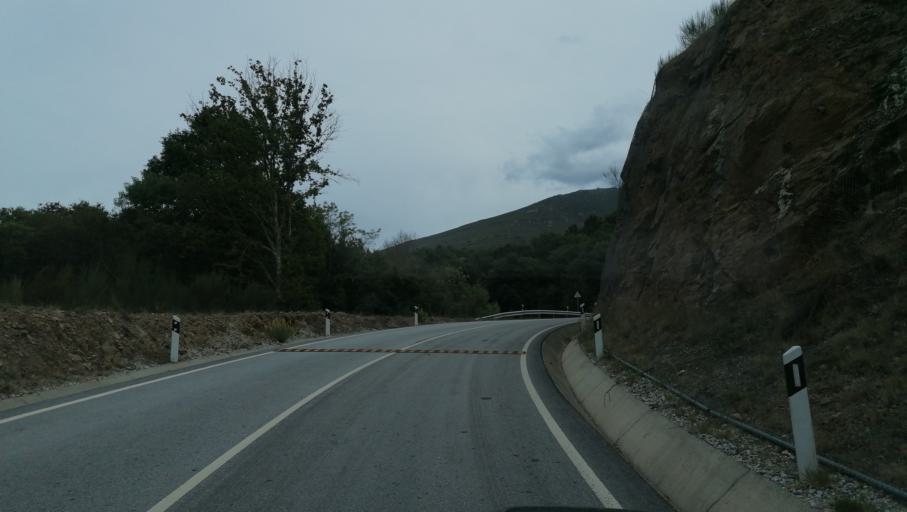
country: PT
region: Vila Real
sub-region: Ribeira de Pena
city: Sobreira
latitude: 41.5650
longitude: -7.7157
